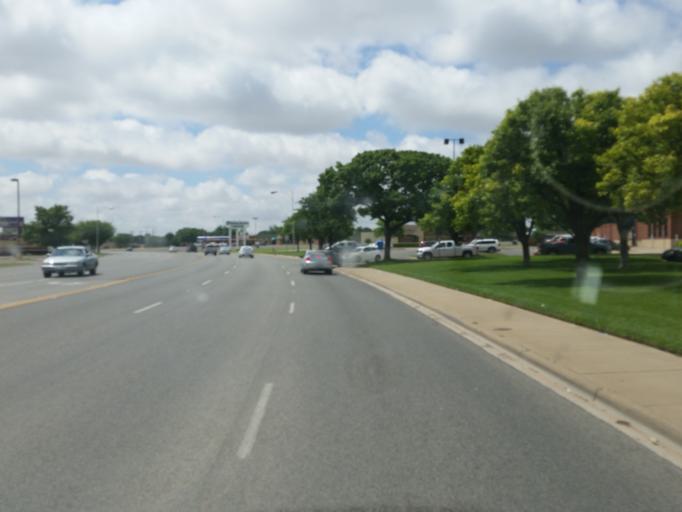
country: US
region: Texas
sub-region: Lubbock County
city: Lubbock
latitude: 33.5485
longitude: -101.8553
